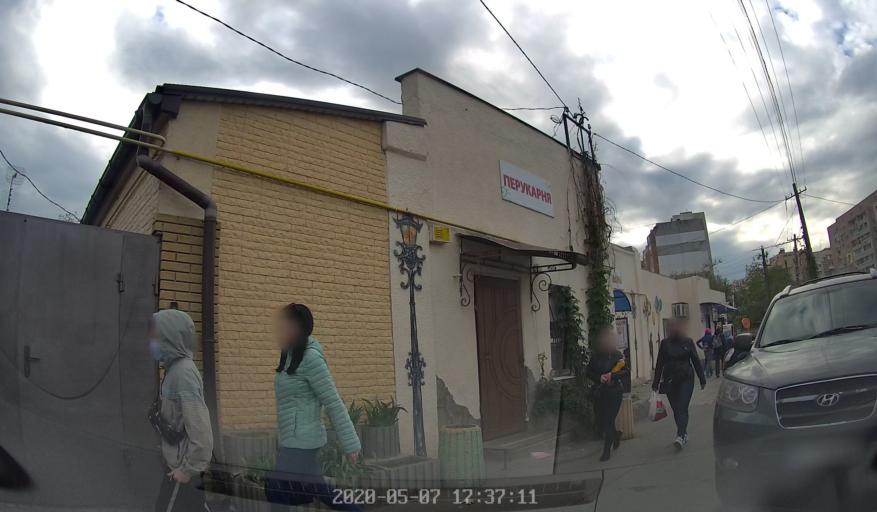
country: NG
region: Niger
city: Lemu
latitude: 9.2773
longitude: 6.1464
